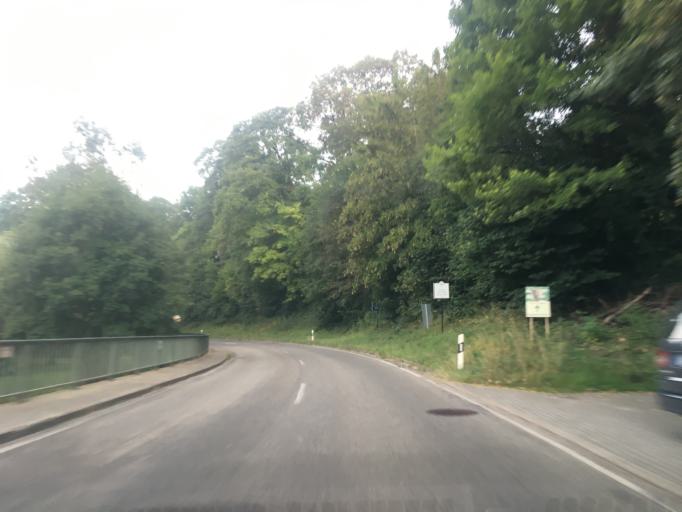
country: DE
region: Baden-Wuerttemberg
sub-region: Tuebingen Region
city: Gomadingen
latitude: 48.3715
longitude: 9.4229
